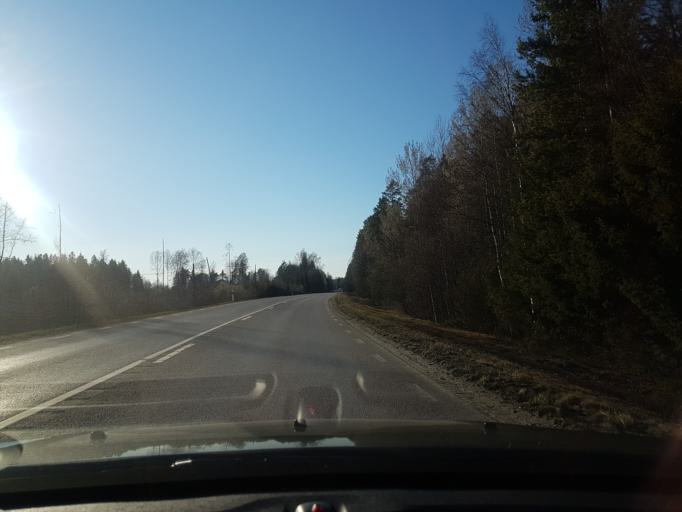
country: SE
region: Uppsala
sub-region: Heby Kommun
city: Morgongava
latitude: 59.8992
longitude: 17.0897
